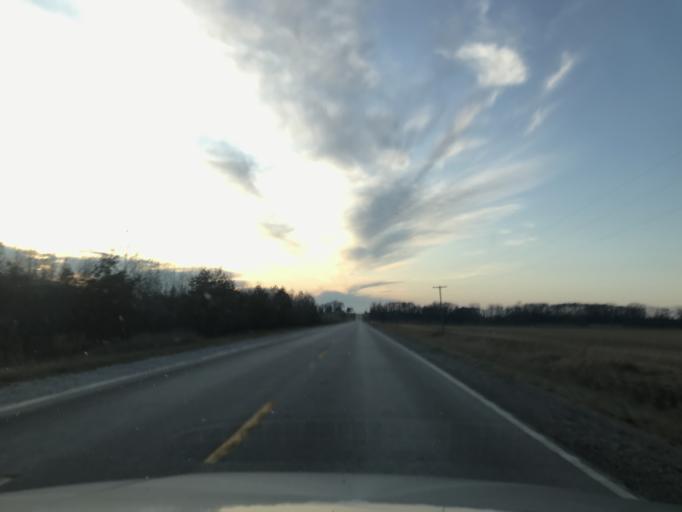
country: US
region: Illinois
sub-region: Henderson County
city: Oquawka
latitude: 41.0190
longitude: -90.8190
